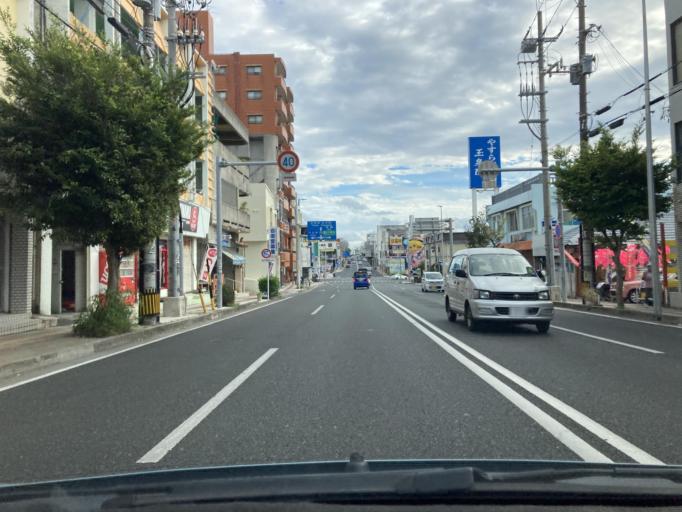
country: JP
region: Okinawa
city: Okinawa
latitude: 26.3404
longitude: 127.8149
